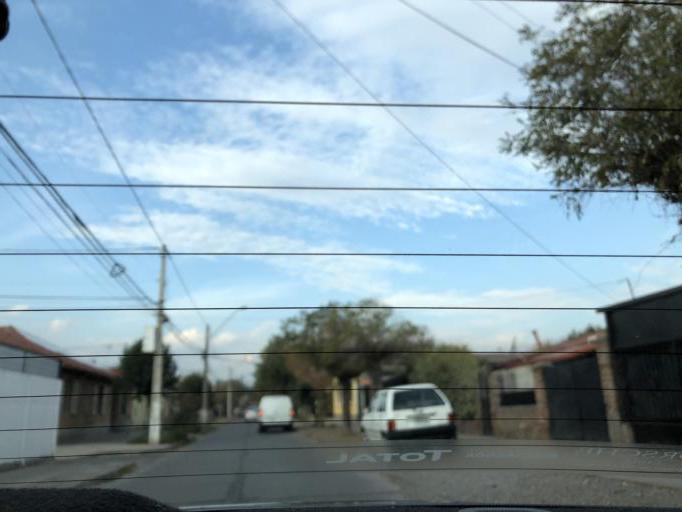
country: CL
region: Santiago Metropolitan
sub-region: Provincia de Cordillera
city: Puente Alto
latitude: -33.6109
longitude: -70.5835
